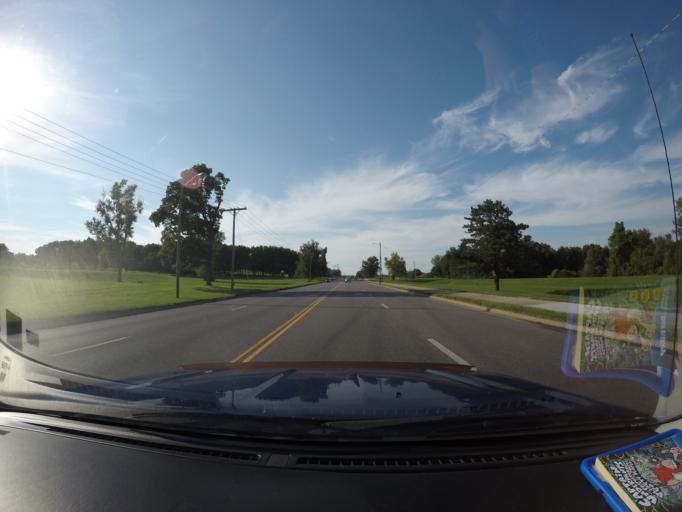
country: US
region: Kansas
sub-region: Leavenworth County
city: Lansing
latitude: 39.2792
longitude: -94.9005
